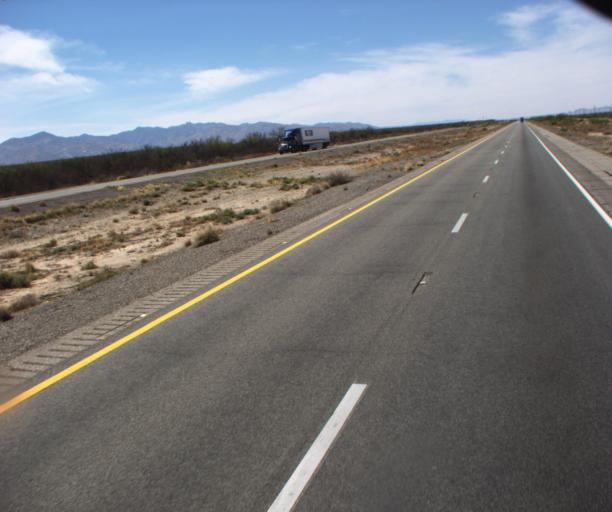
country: US
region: Arizona
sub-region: Cochise County
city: Willcox
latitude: 32.2894
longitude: -109.3188
